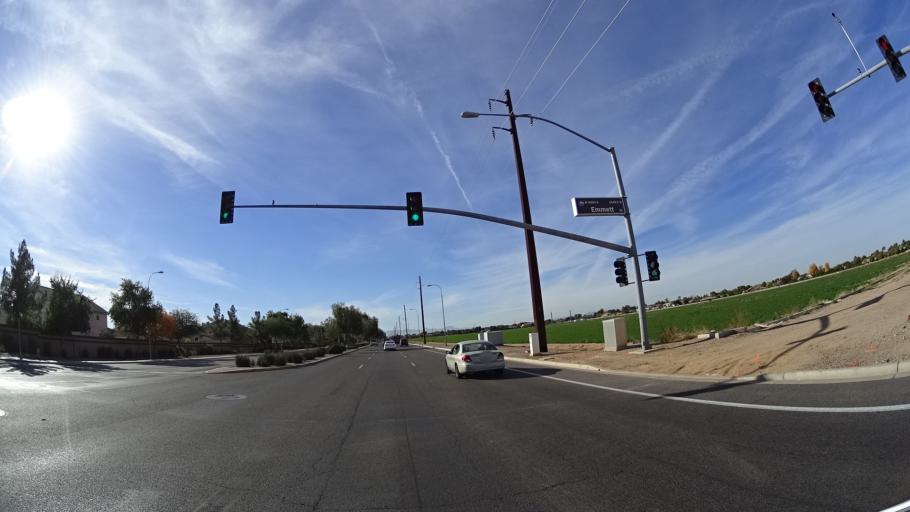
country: US
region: Arizona
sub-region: Maricopa County
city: Sun Lakes
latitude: 33.2192
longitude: -111.7979
